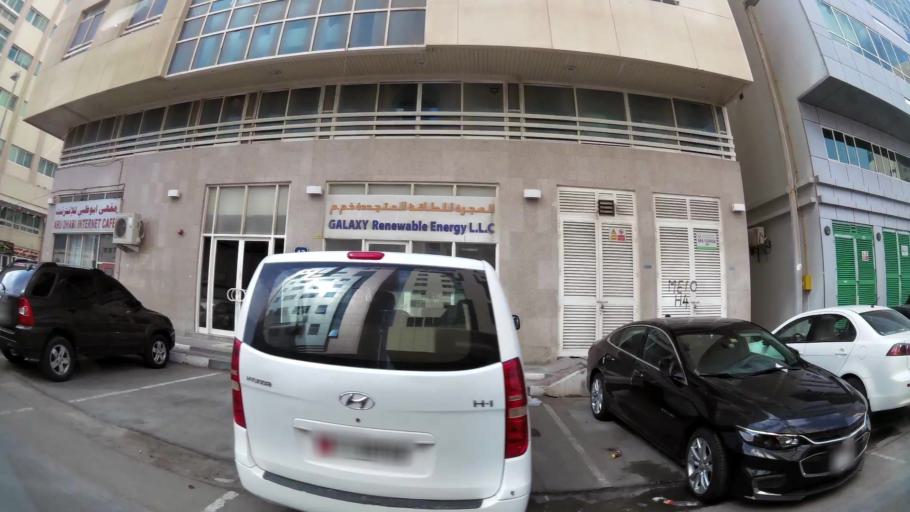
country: AE
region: Abu Dhabi
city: Abu Dhabi
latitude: 24.3363
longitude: 54.5315
